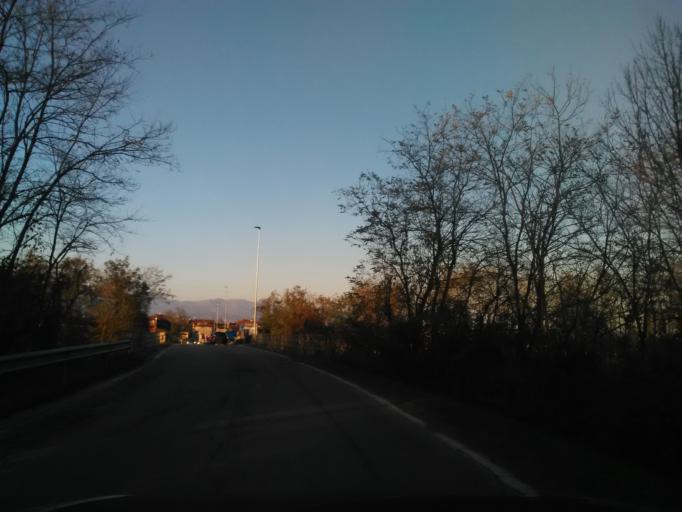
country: IT
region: Piedmont
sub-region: Provincia di Biella
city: Cerrione
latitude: 45.4651
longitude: 8.0696
